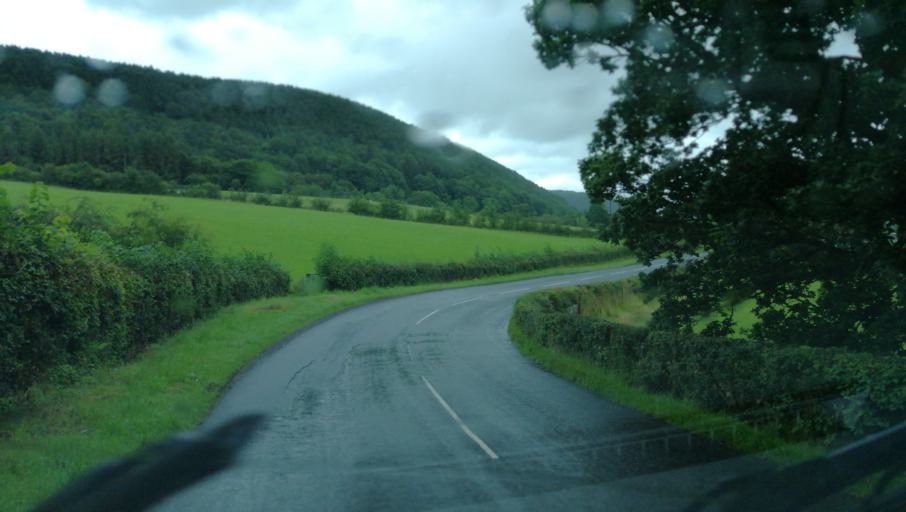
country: GB
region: England
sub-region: Cumbria
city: Penrith
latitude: 54.6024
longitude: -2.8511
